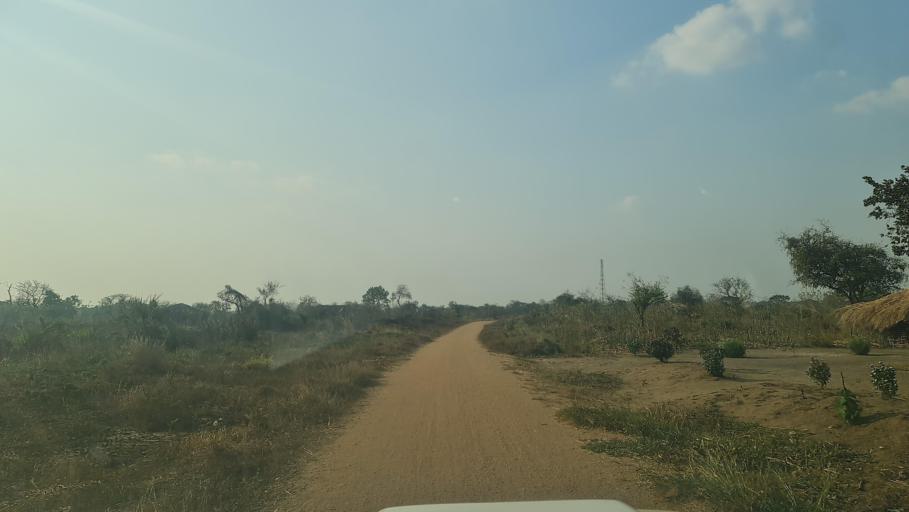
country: MZ
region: Zambezia
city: Quelimane
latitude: -18.1501
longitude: 35.9882
